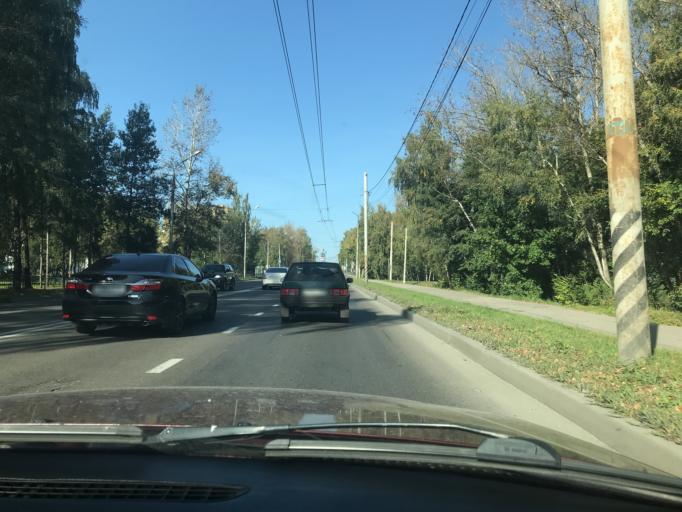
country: RU
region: Kaluga
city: Kaluga
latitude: 54.5798
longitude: 36.2548
